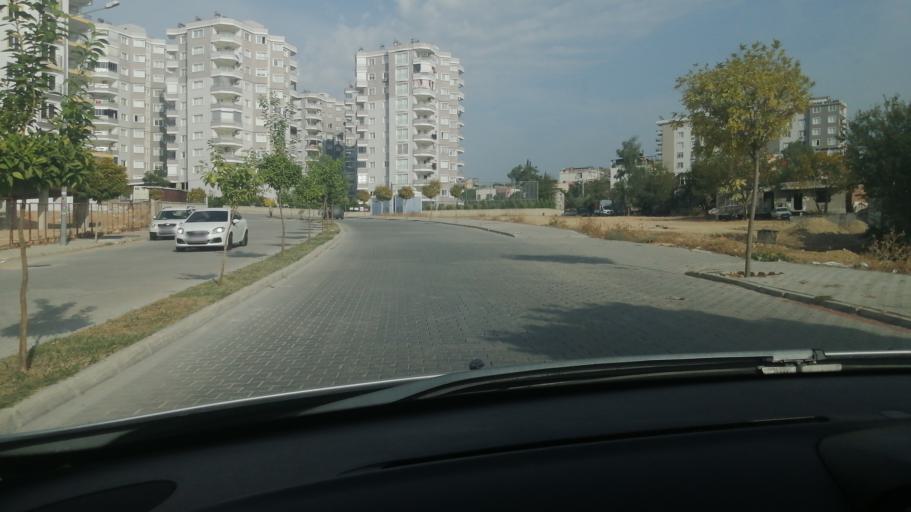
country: TR
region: Adana
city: Kadirli
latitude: 37.3724
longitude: 36.0820
